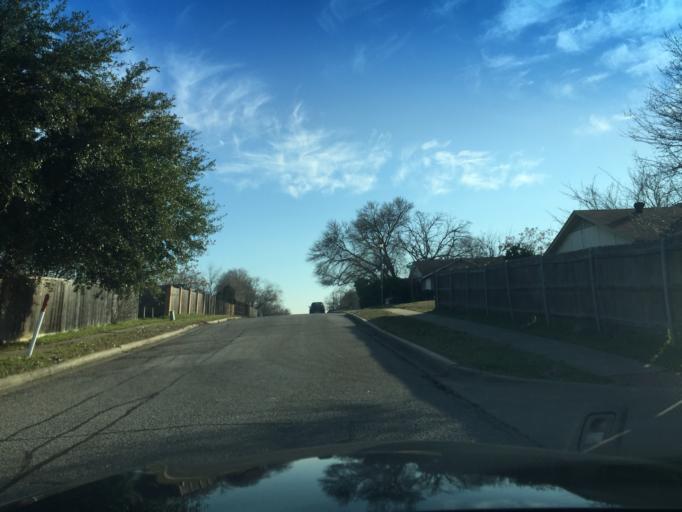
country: US
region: Texas
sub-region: Dallas County
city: Carrollton
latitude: 32.9894
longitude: -96.8801
